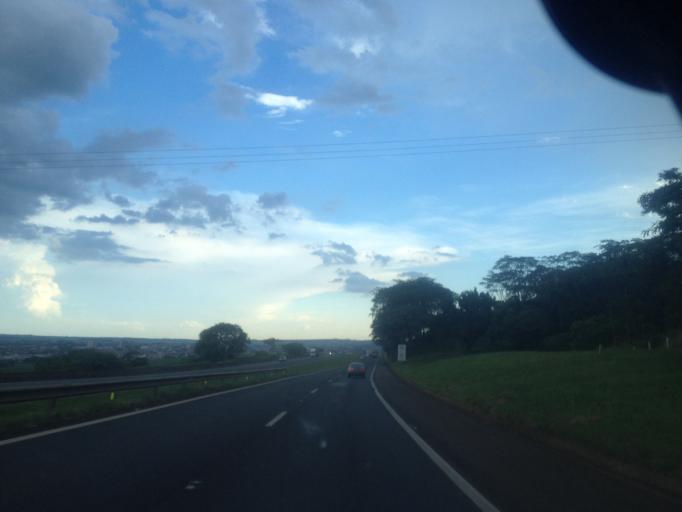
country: BR
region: Sao Paulo
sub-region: Leme
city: Leme
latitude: -22.1541
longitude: -47.4003
